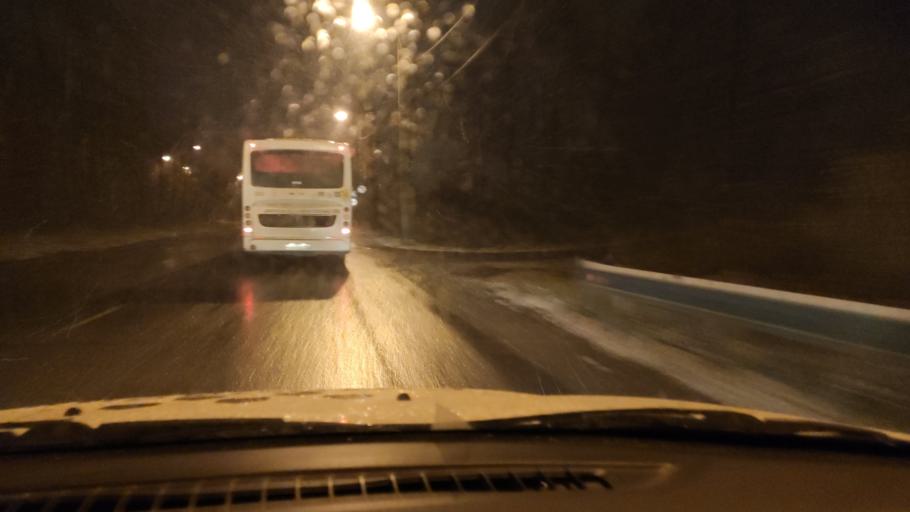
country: RU
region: Perm
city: Kondratovo
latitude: 57.9685
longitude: 56.1277
